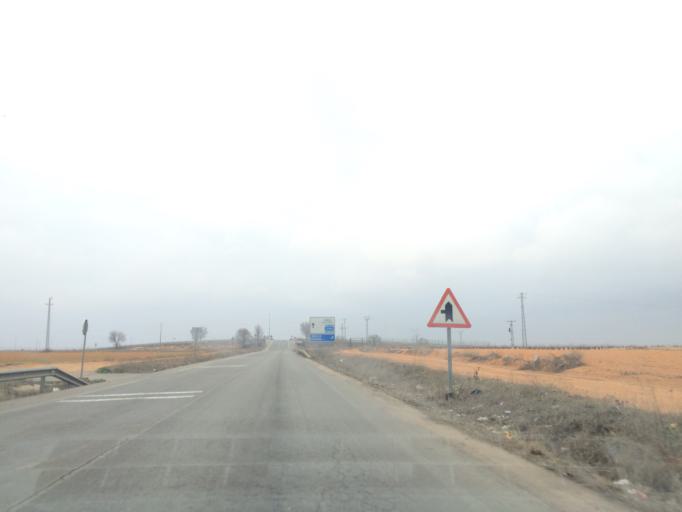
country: ES
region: Castille-La Mancha
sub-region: Province of Toledo
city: Madridejos
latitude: 39.4765
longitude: -3.5262
